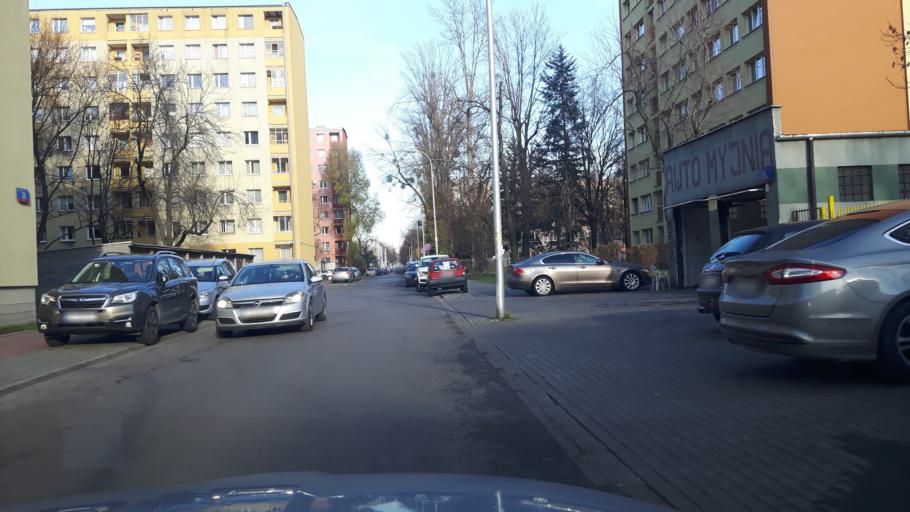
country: PL
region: Masovian Voivodeship
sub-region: Warszawa
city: Ochota
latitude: 52.2040
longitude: 20.9723
